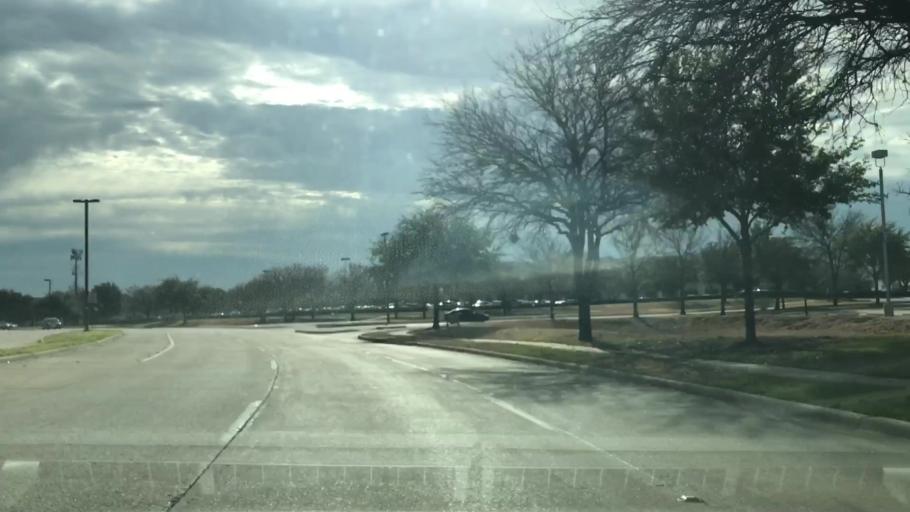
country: US
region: Texas
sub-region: Dallas County
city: Coppell
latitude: 32.9218
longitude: -96.9986
